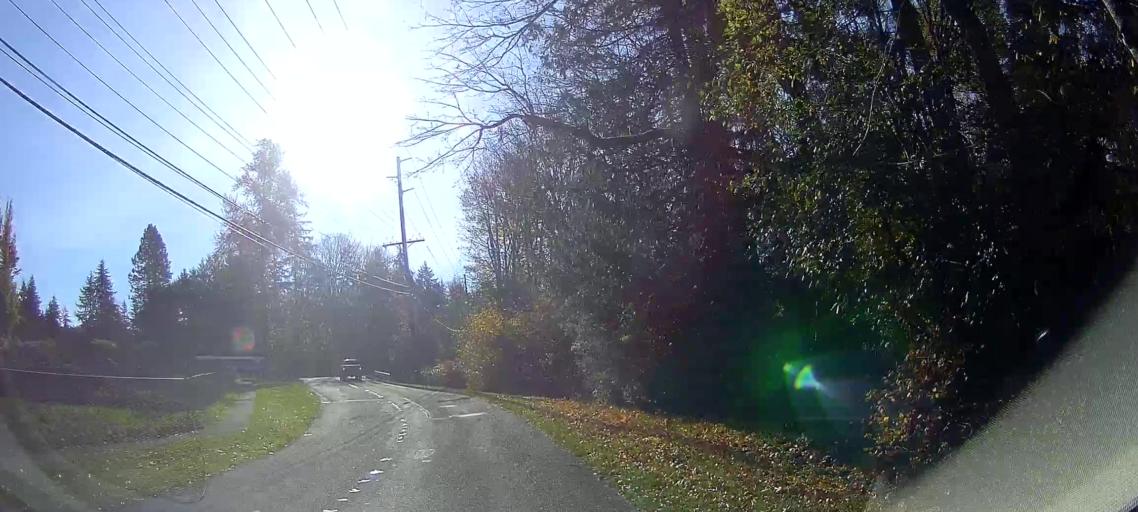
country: US
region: Washington
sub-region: Whatcom County
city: Geneva
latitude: 48.7460
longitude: -122.4453
